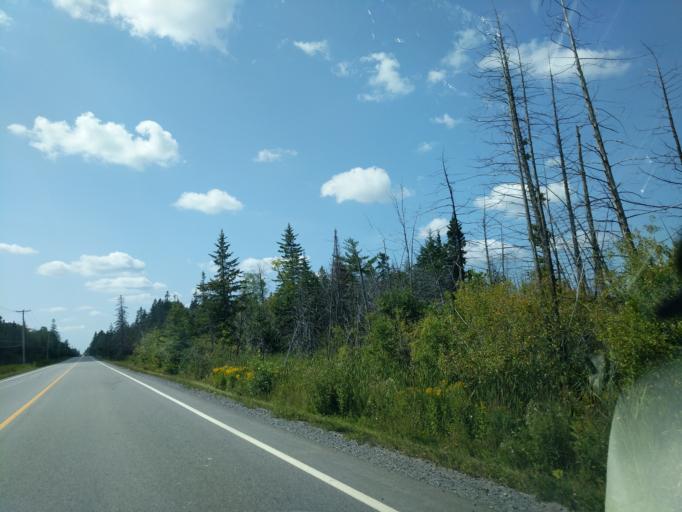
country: CA
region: Ontario
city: Bells Corners
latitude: 45.4414
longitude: -75.8245
